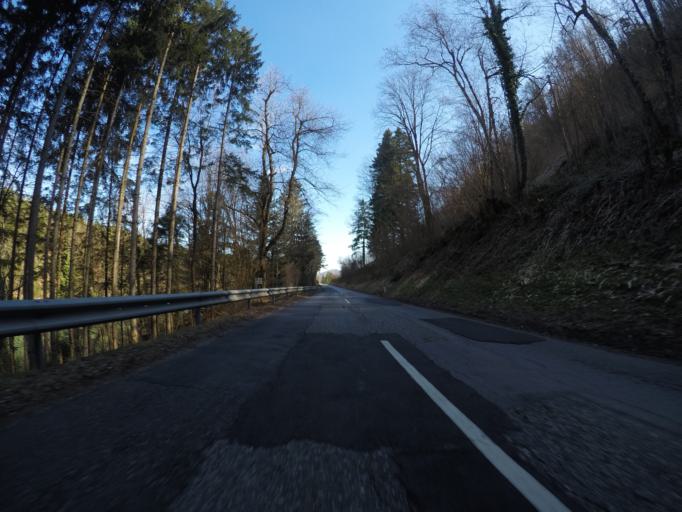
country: SI
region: Selnica ob Dravi
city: Selnica ob Dravi
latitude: 46.5329
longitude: 15.4624
